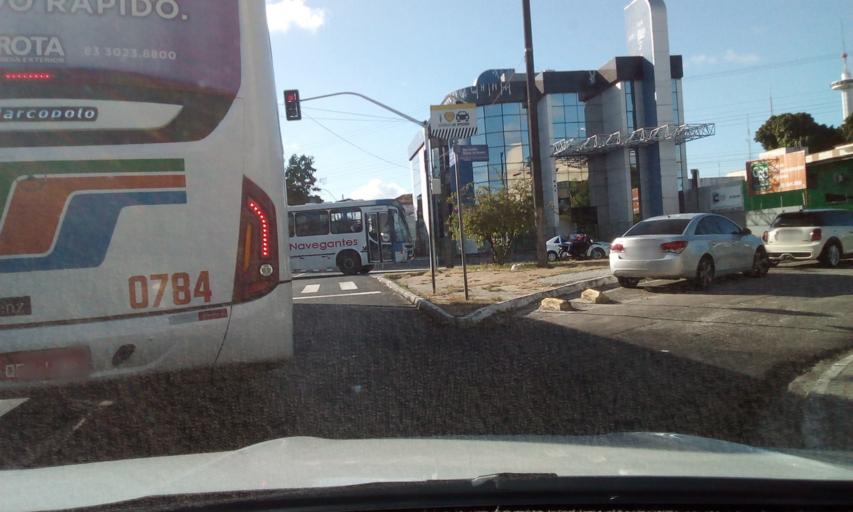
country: BR
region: Paraiba
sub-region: Joao Pessoa
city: Joao Pessoa
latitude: -7.1204
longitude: -34.8736
